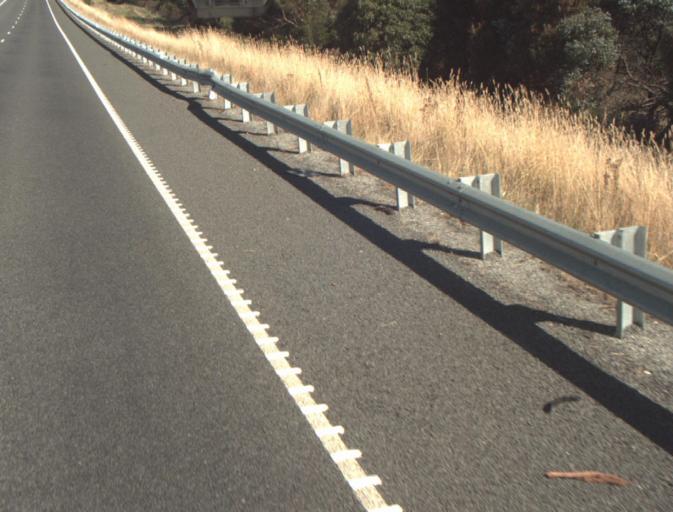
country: AU
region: Tasmania
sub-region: Launceston
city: Mayfield
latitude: -41.3633
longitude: 147.1075
